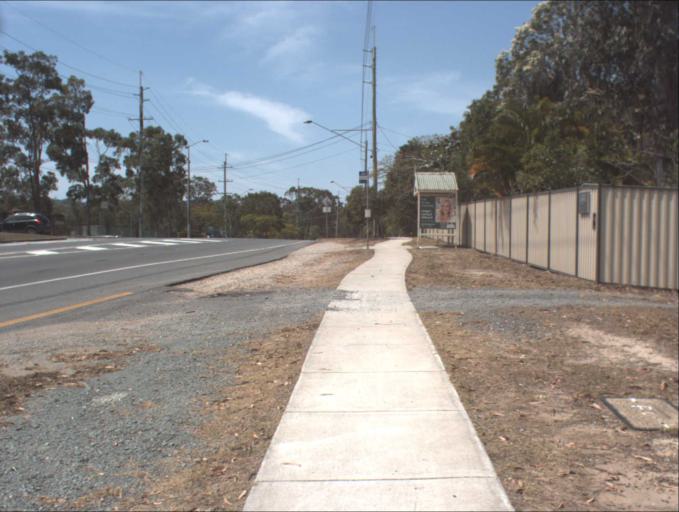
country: AU
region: Queensland
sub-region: Logan
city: Beenleigh
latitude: -27.6678
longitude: 153.2046
